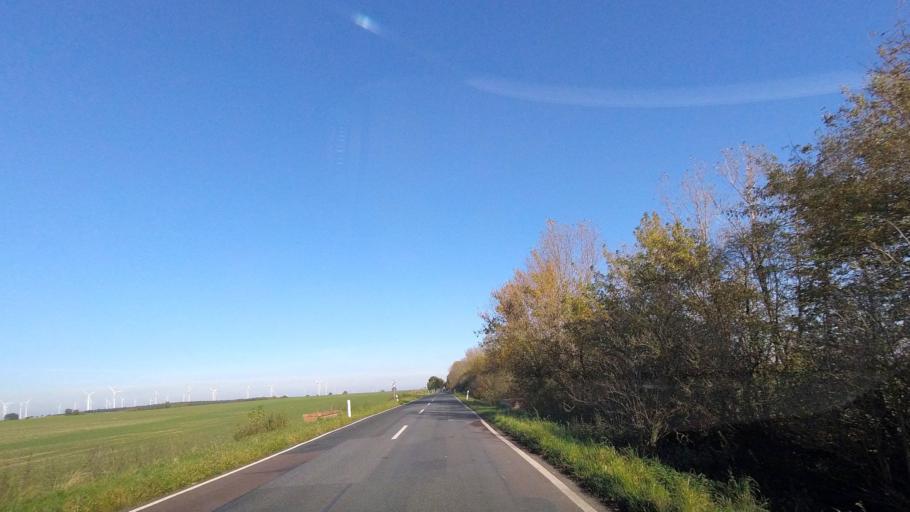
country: DE
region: Brandenburg
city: Treuenbrietzen
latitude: 51.9912
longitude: 12.8729
